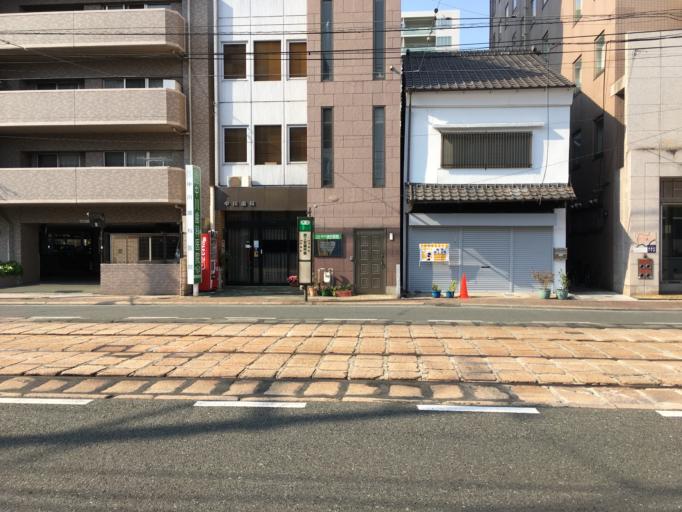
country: JP
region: Kumamoto
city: Kumamoto
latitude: 32.7955
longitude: 130.6991
